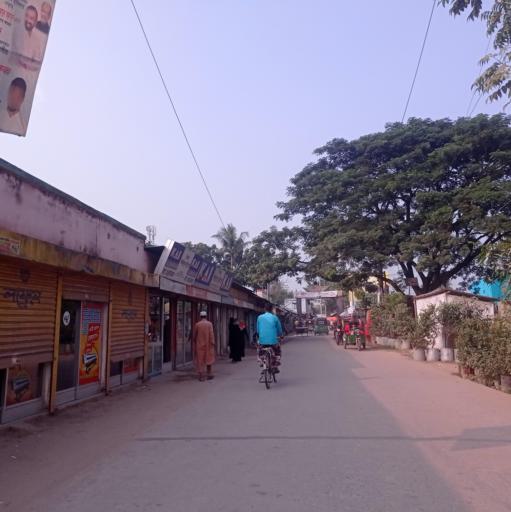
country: BD
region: Dhaka
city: Bhairab Bazar
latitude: 24.1029
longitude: 90.8523
